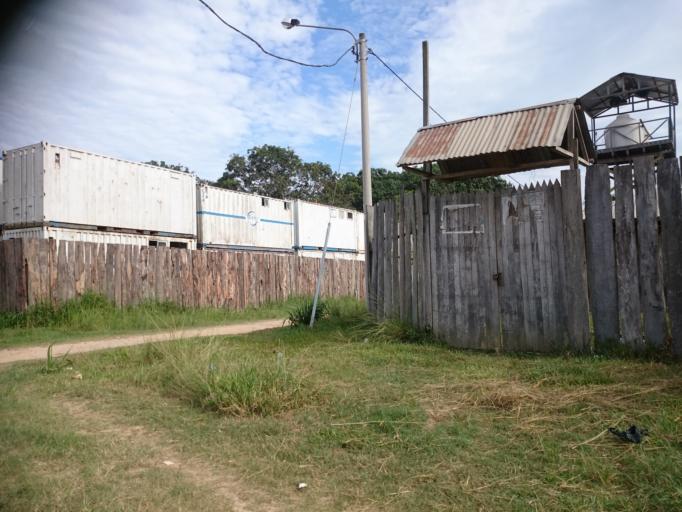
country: PE
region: Ucayali
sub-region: Provincia de Coronel Portillo
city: Puerto Callao
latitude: -8.3904
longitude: -74.5931
